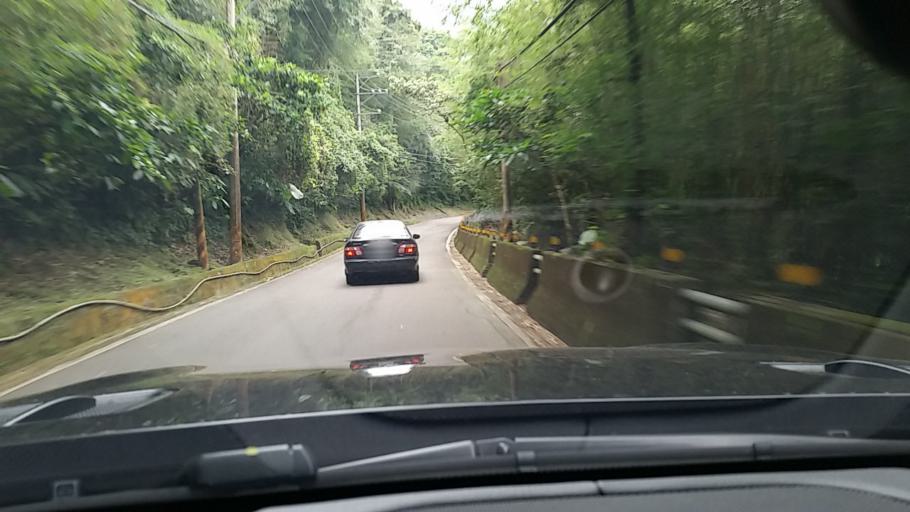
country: TW
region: Taiwan
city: Daxi
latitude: 24.7994
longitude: 121.3034
